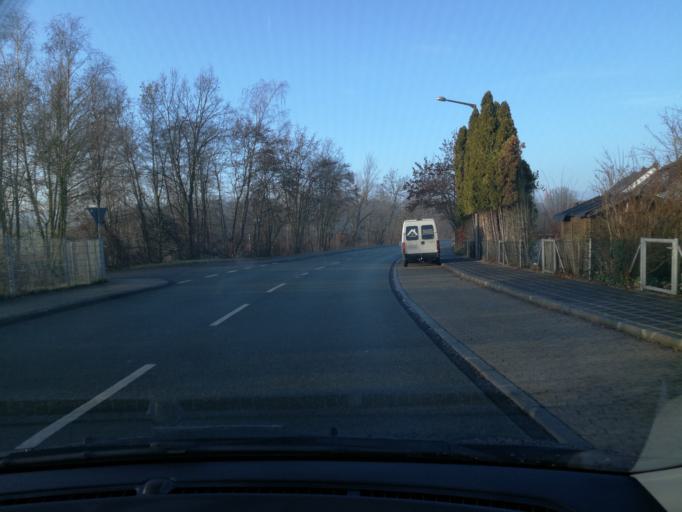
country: DE
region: Bavaria
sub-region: Regierungsbezirk Mittelfranken
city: Zirndorf
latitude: 49.4883
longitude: 10.9387
